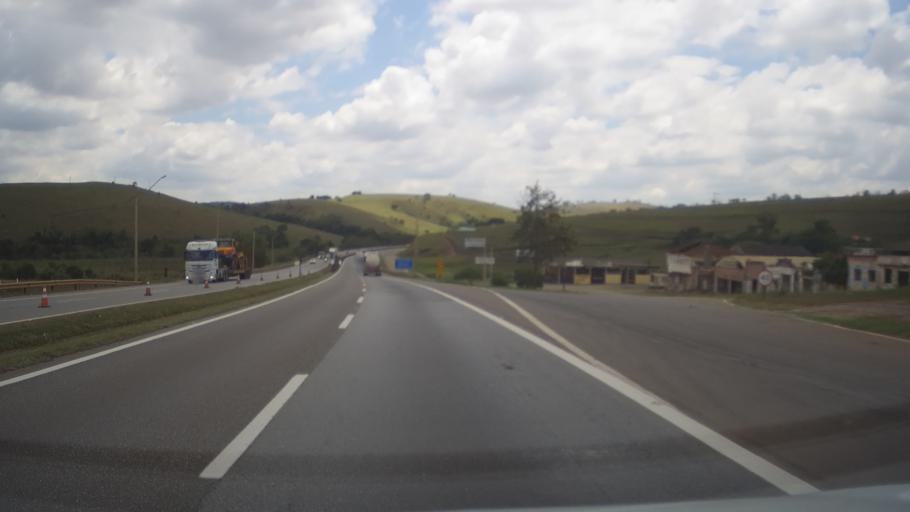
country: BR
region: Minas Gerais
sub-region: Tres Coracoes
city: Tres Coracoes
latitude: -21.7133
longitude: -45.3761
